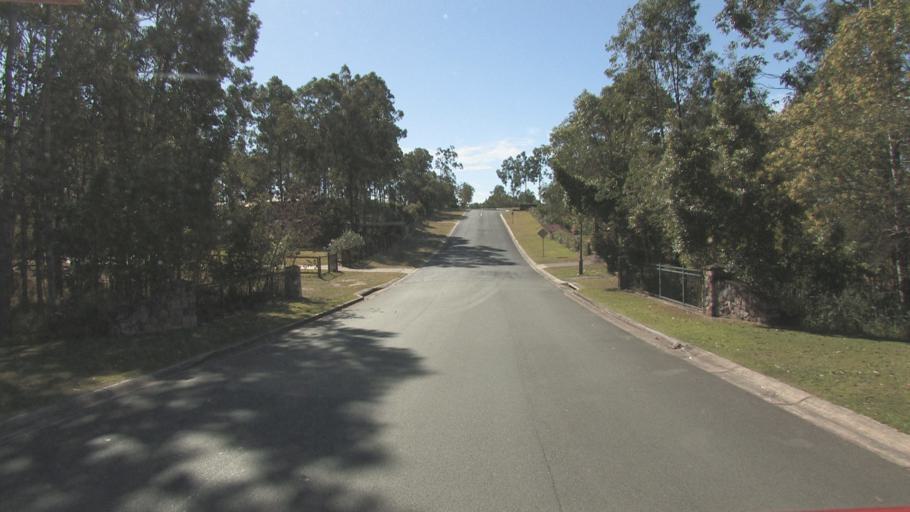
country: AU
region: Queensland
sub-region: Ipswich
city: Springfield Lakes
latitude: -27.7387
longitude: 152.9189
